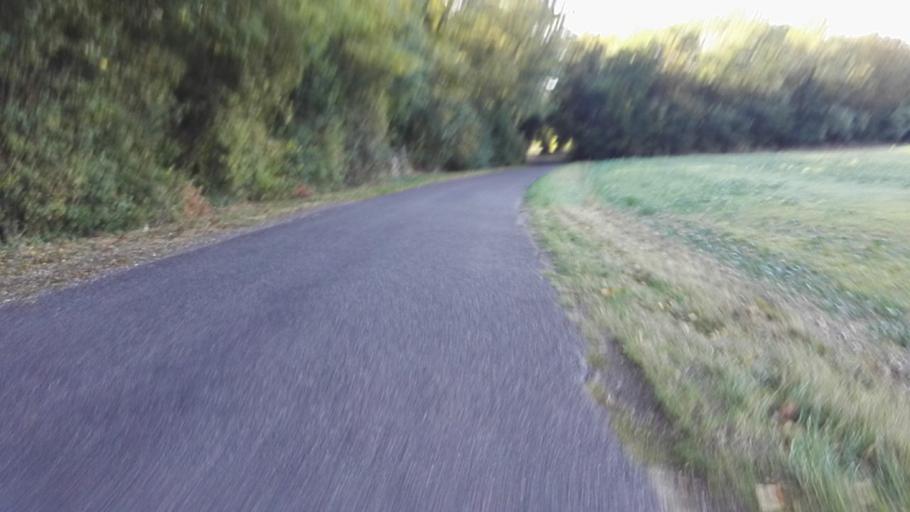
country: FR
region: Haute-Normandie
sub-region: Departement de l'Eure
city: Menilles
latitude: 49.0509
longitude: 1.3363
